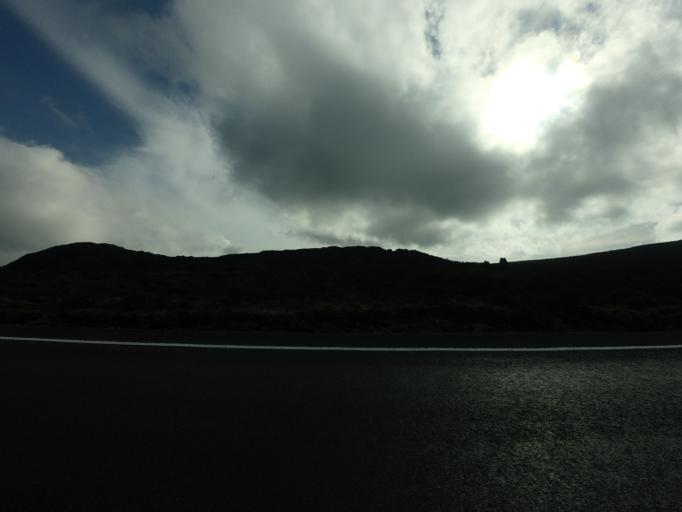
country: AU
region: Tasmania
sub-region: Meander Valley
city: Deloraine
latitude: -41.7318
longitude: 146.7078
